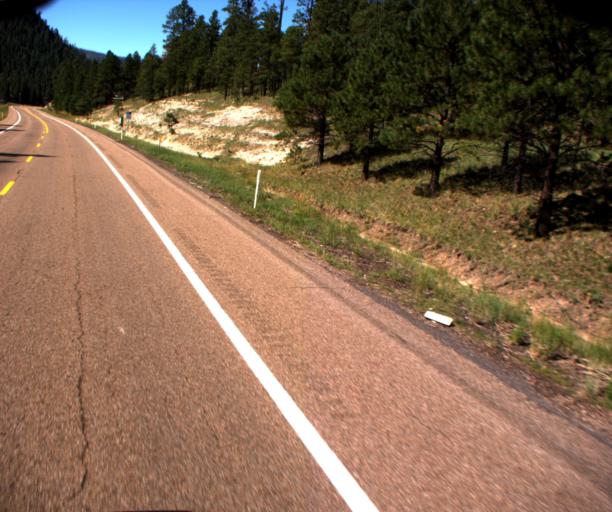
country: US
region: Arizona
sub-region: Apache County
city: Eagar
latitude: 33.8880
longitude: -109.1573
